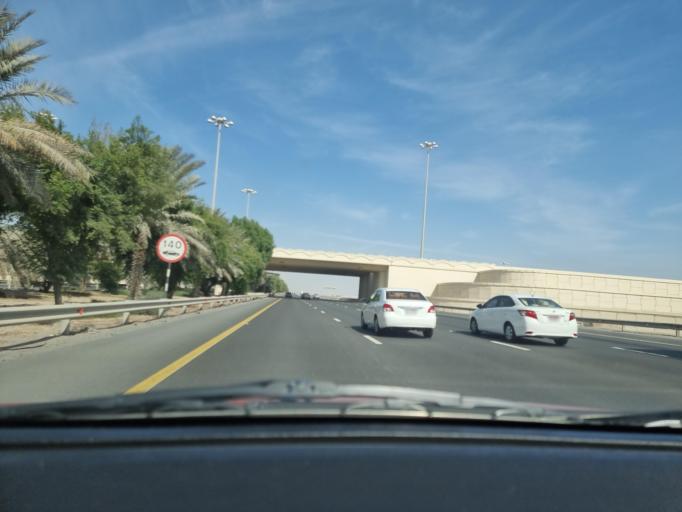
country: AE
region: Abu Dhabi
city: Abu Dhabi
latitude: 24.3389
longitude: 54.6361
